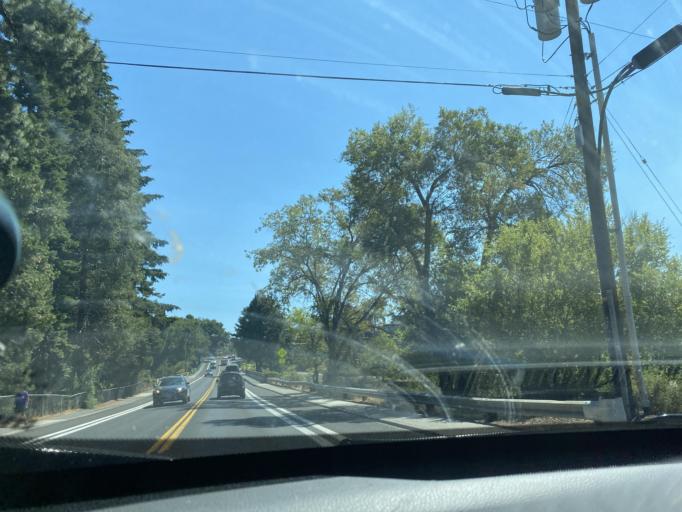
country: US
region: Oregon
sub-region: Deschutes County
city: Bend
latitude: 44.0642
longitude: -121.3121
